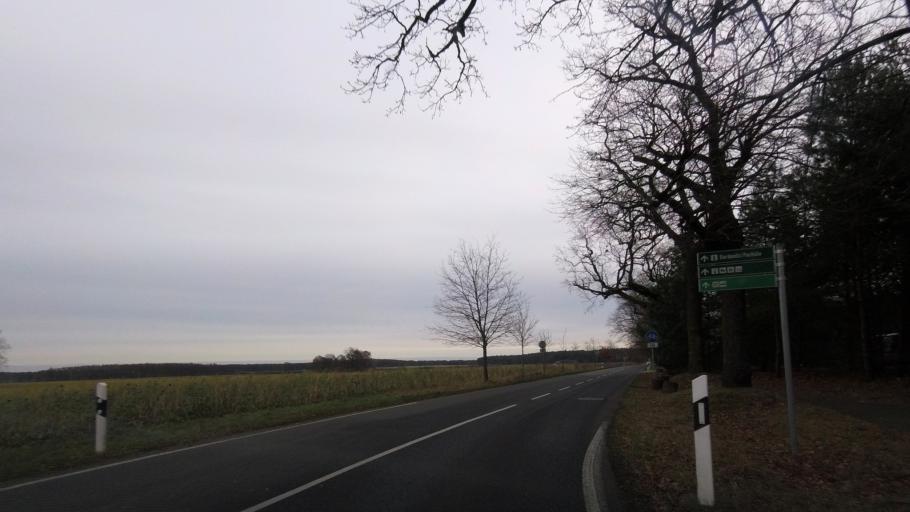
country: DE
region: Brandenburg
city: Treuenbrietzen
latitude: 52.0797
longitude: 12.8823
